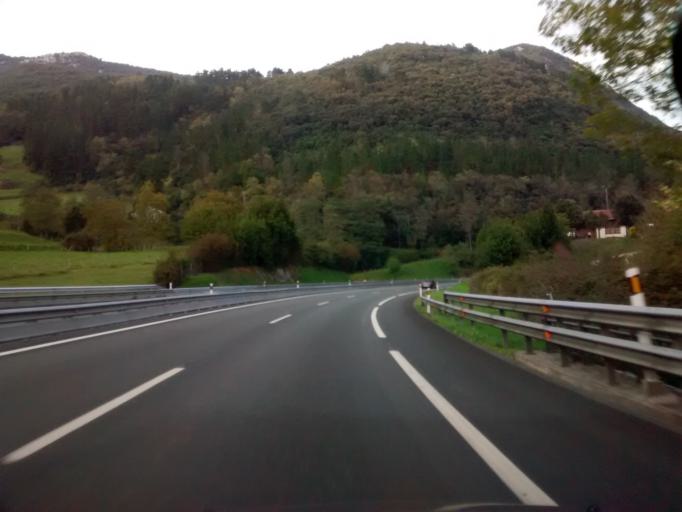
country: ES
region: Basque Country
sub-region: Provincia de Guipuzcoa
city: Mendaro
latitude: 43.2544
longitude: -2.3899
